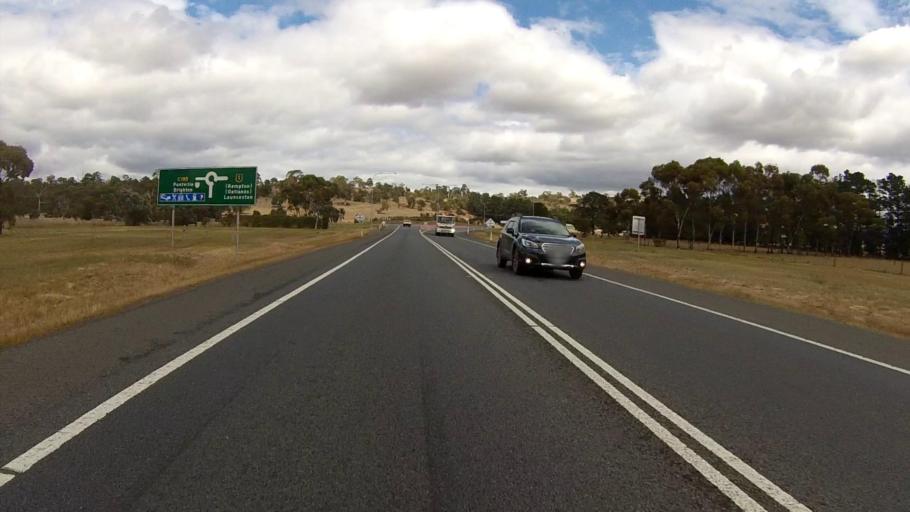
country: AU
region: Tasmania
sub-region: Brighton
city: Bridgewater
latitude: -42.6725
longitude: 147.2624
